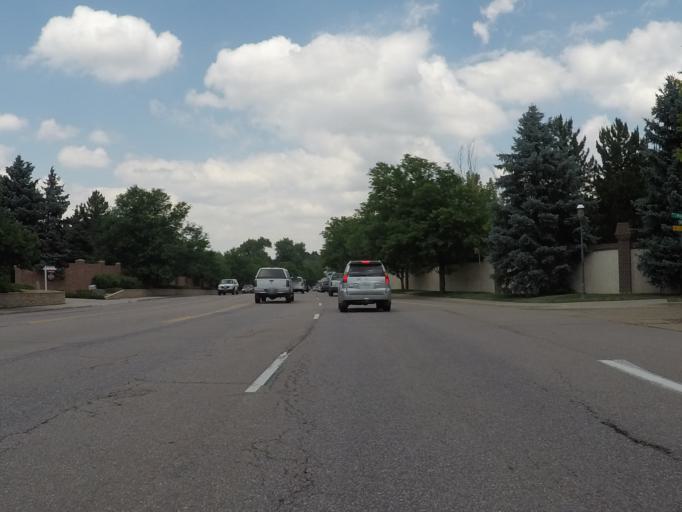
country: US
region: Colorado
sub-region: Arapahoe County
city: Greenwood Village
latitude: 39.6198
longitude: -104.9597
